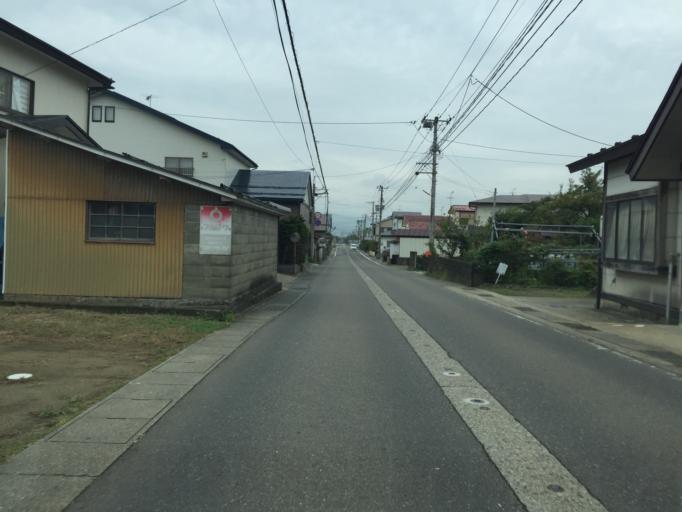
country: JP
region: Fukushima
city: Kitakata
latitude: 37.5443
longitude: 139.9285
